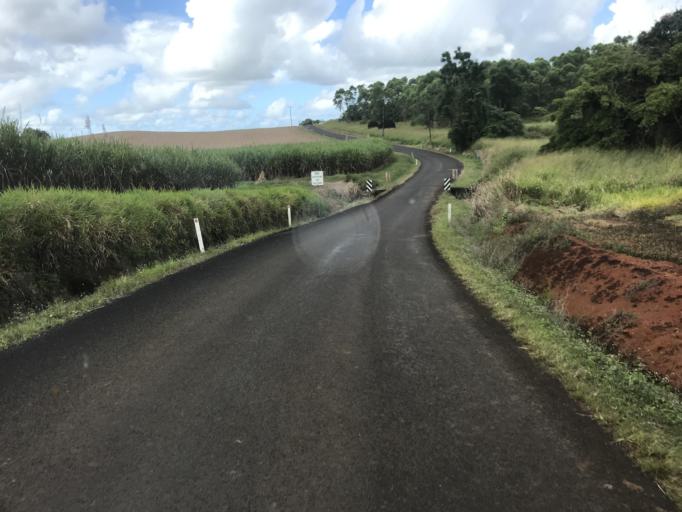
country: AU
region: Queensland
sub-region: Cassowary Coast
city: Innisfail
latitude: -17.5525
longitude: 145.8819
